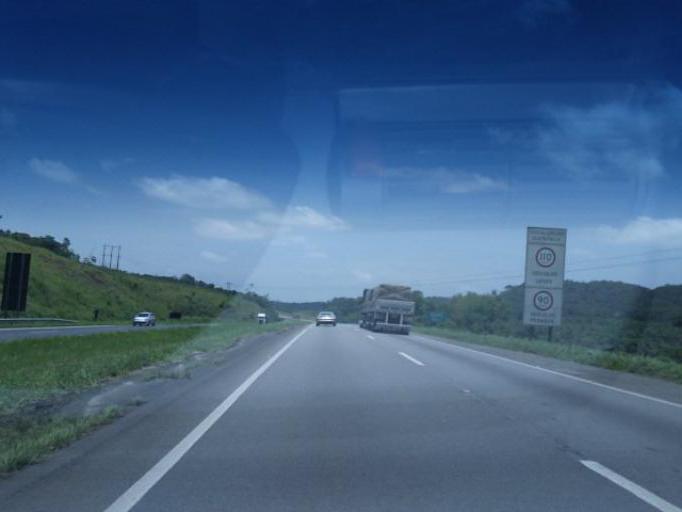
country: BR
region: Sao Paulo
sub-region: Miracatu
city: Miracatu
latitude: -24.2921
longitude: -47.4715
